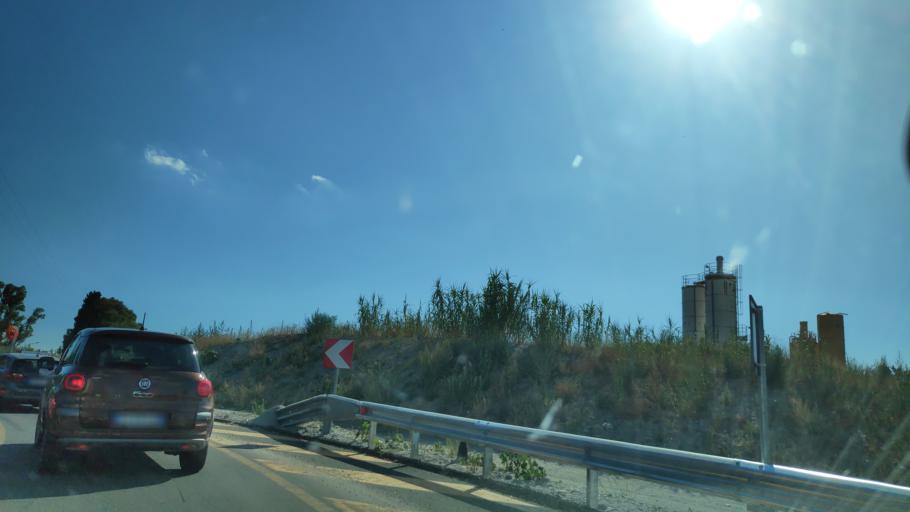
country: IT
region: Calabria
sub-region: Provincia di Reggio Calabria
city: Caulonia Marina
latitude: 38.3488
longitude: 16.4702
